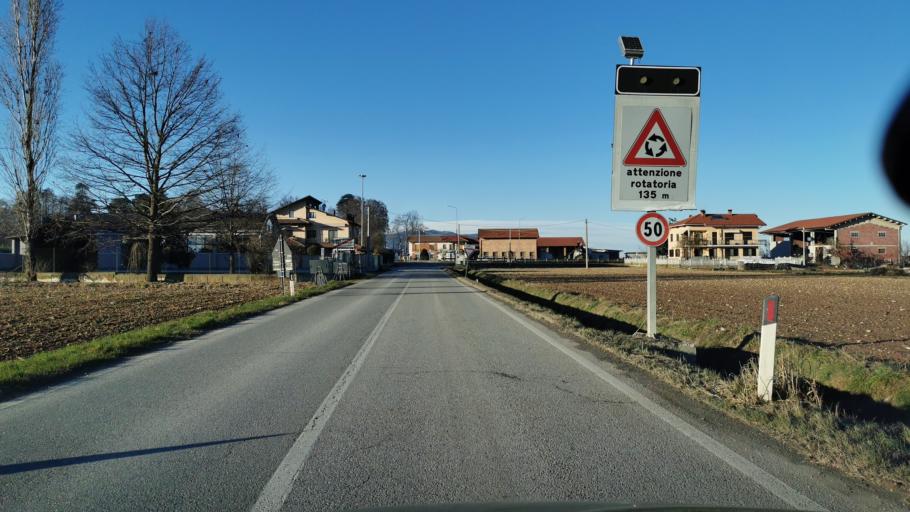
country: IT
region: Piedmont
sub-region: Provincia di Cuneo
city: Roata Rossi
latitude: 44.4554
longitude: 7.4895
